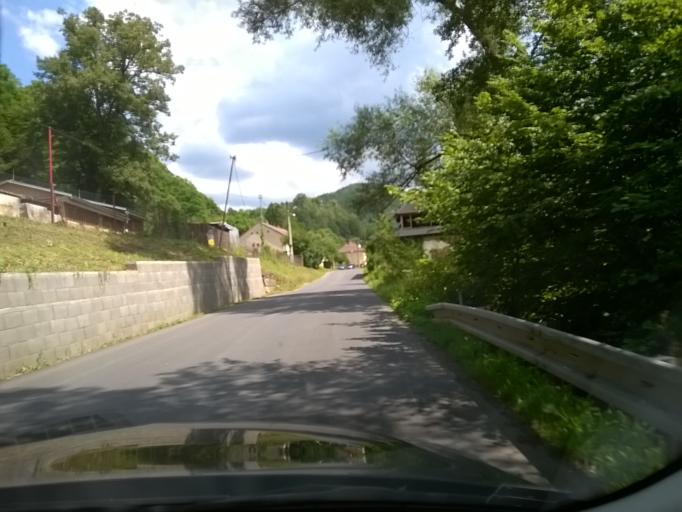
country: SK
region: Banskobystricky
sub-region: Okres Banska Bystrica
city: Banska Stiavnica
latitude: 48.4568
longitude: 18.8119
